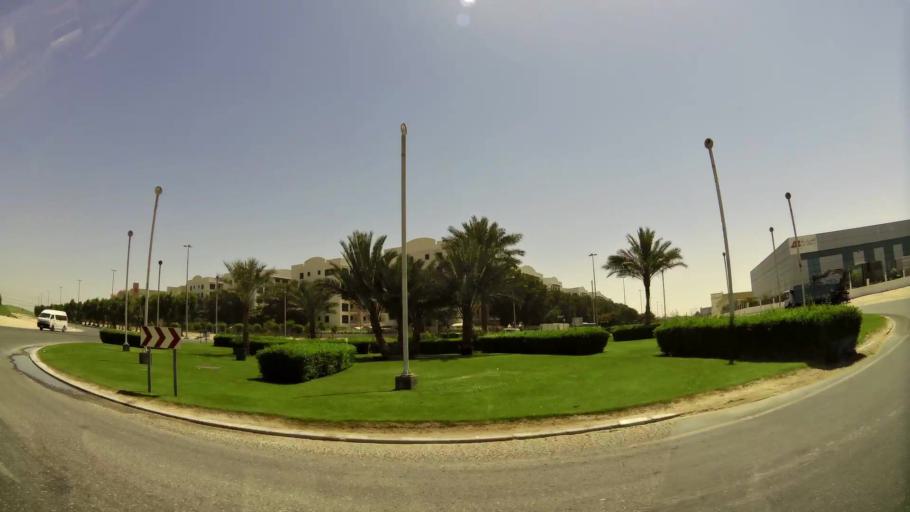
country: AE
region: Dubai
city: Dubai
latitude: 24.9844
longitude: 55.2003
